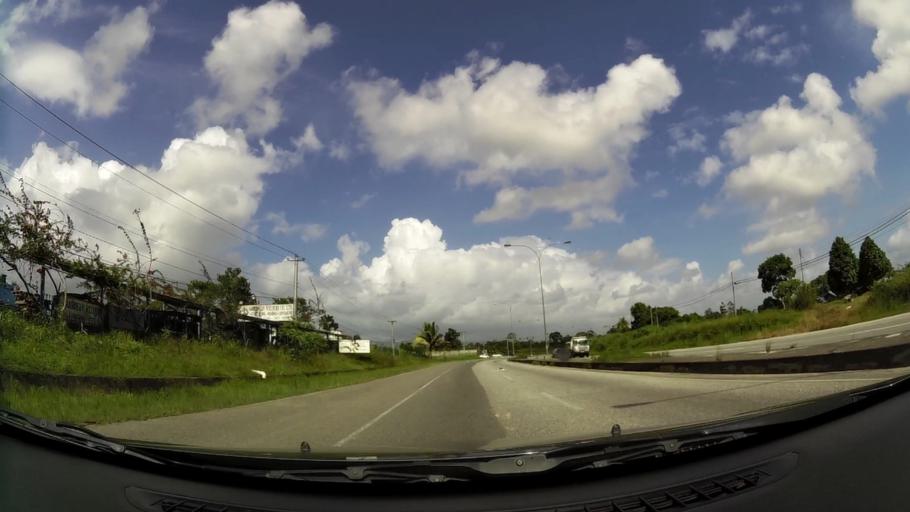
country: TT
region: Borough of Arima
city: Arima
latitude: 10.6193
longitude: -61.2552
